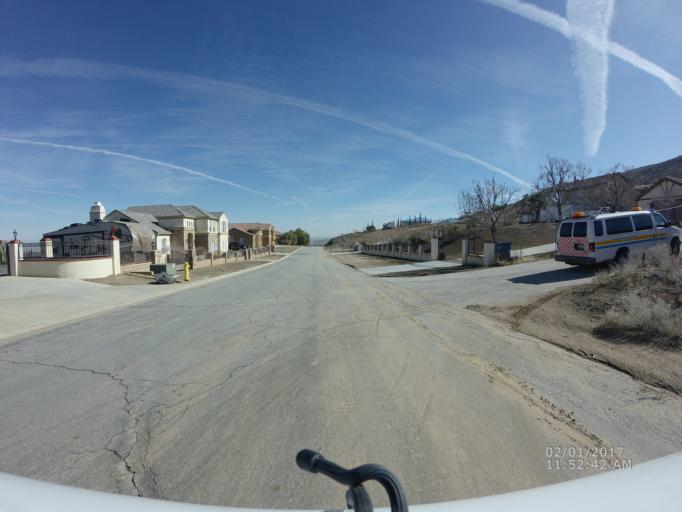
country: US
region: California
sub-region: Los Angeles County
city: Palmdale
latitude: 34.5422
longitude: -118.1361
